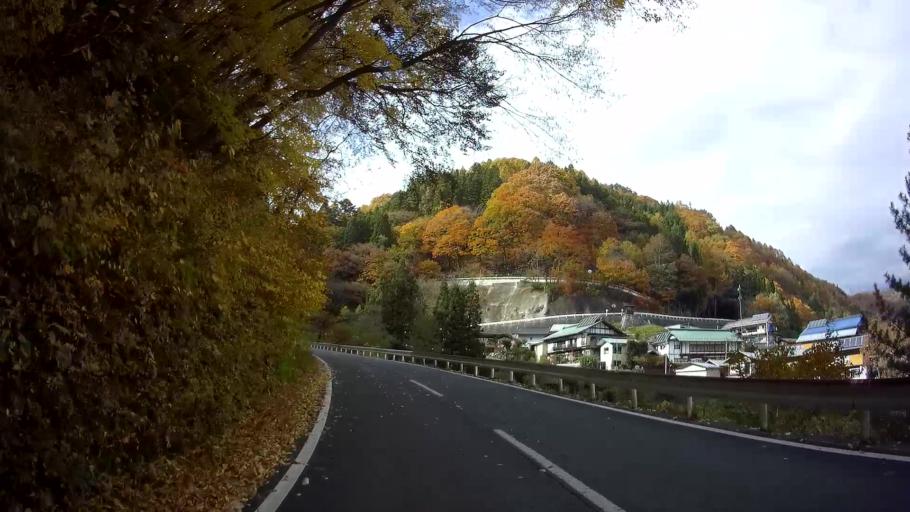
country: JP
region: Gunma
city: Nakanojomachi
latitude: 36.6155
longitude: 138.6402
